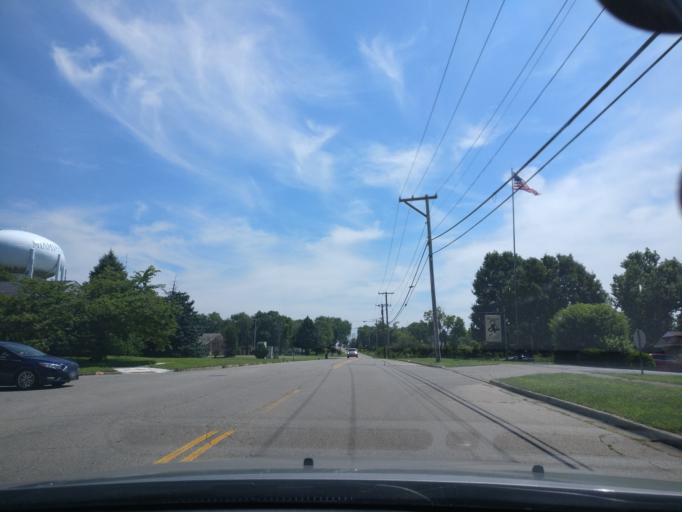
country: US
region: Ohio
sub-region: Montgomery County
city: West Carrollton City
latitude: 39.6419
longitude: -84.2511
